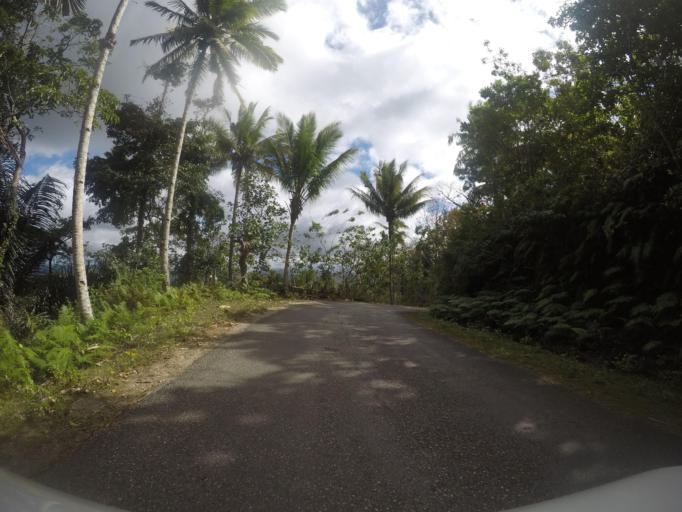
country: TL
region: Lautem
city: Lospalos
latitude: -8.5340
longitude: 126.9326
